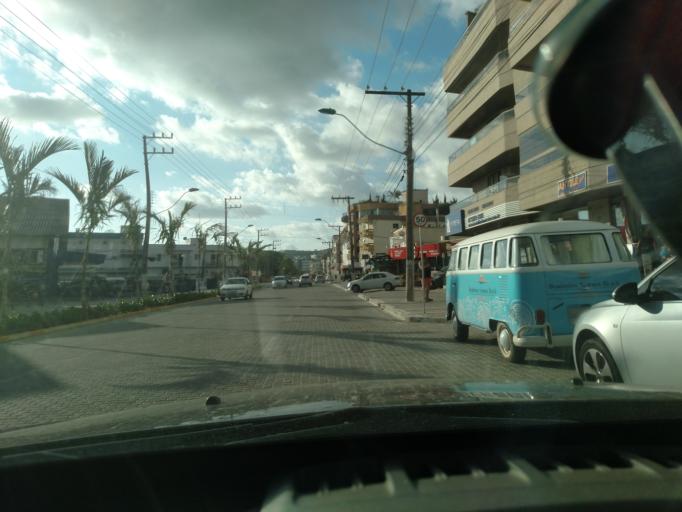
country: BR
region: Santa Catarina
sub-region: Porto Belo
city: Porto Belo
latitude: -27.1379
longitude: -48.5110
